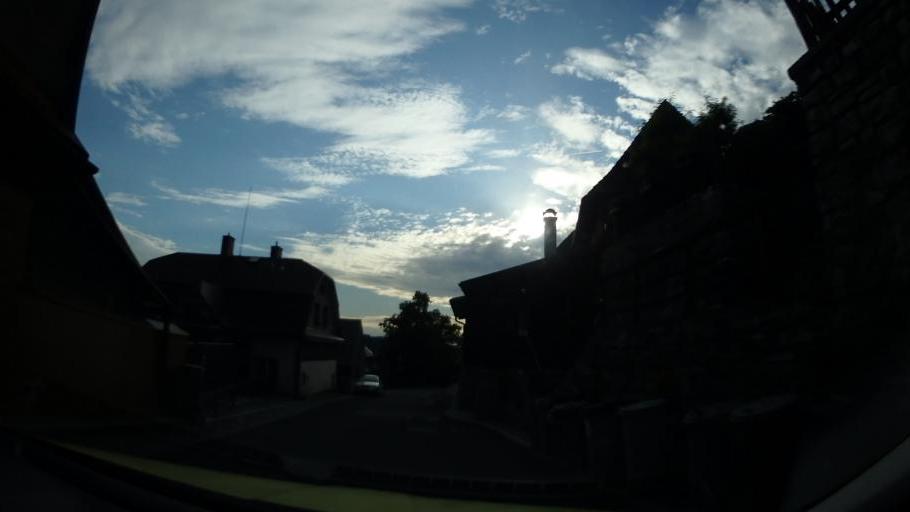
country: CZ
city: Stramberk
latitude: 49.5906
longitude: 18.1159
